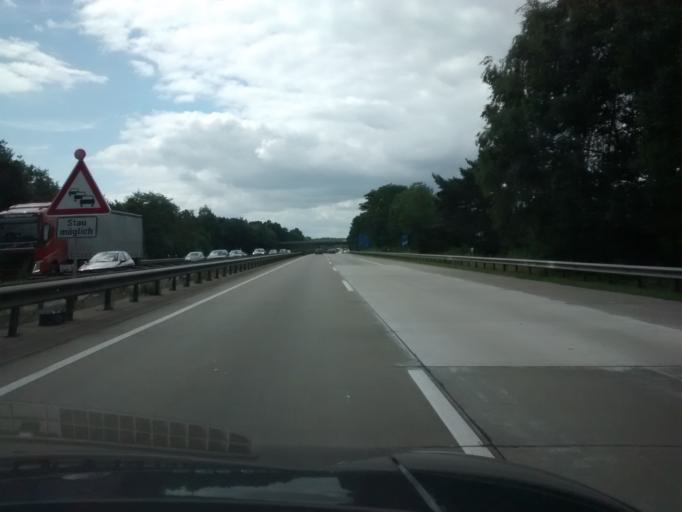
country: DE
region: Lower Saxony
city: Gross Ippener
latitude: 52.9756
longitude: 8.6221
